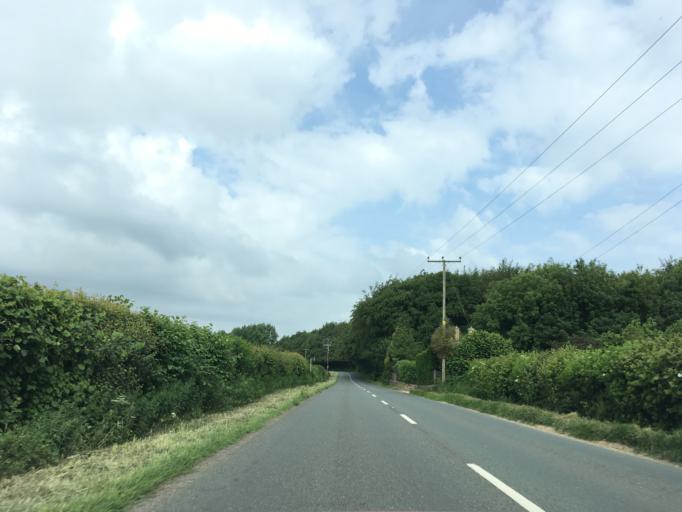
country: GB
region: England
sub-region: Gloucestershire
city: Nailsworth
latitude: 51.6551
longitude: -2.2453
